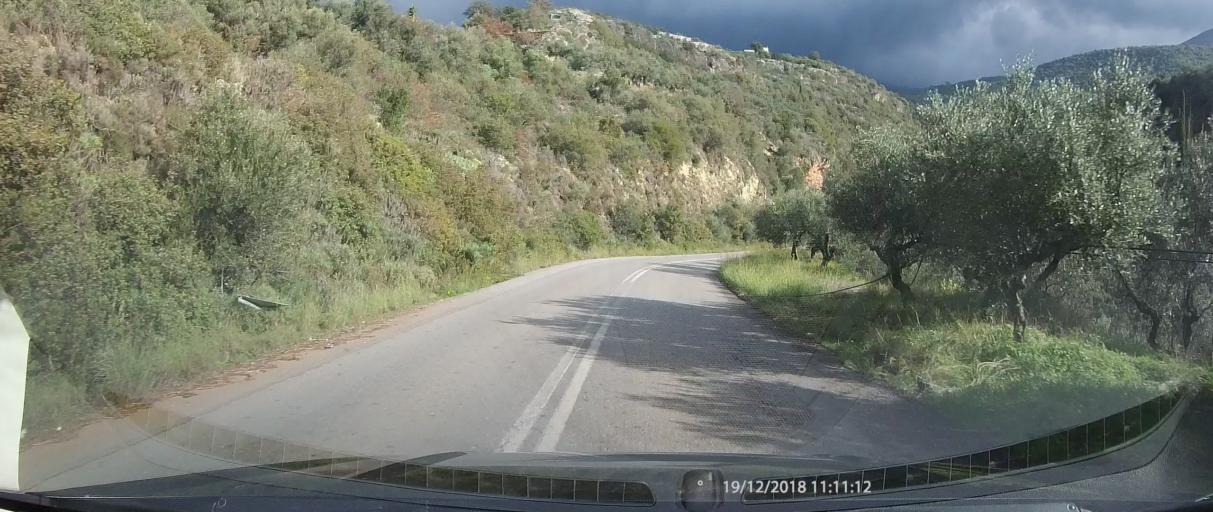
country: GR
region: Peloponnese
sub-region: Nomos Messinias
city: Kardamyli
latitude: 36.8205
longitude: 22.3019
